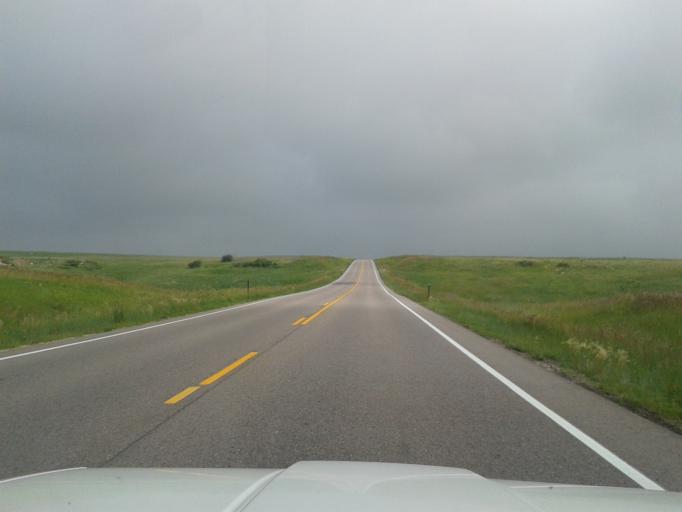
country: US
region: Colorado
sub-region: Elbert County
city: Ponderosa Park
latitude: 39.2986
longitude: -104.7359
